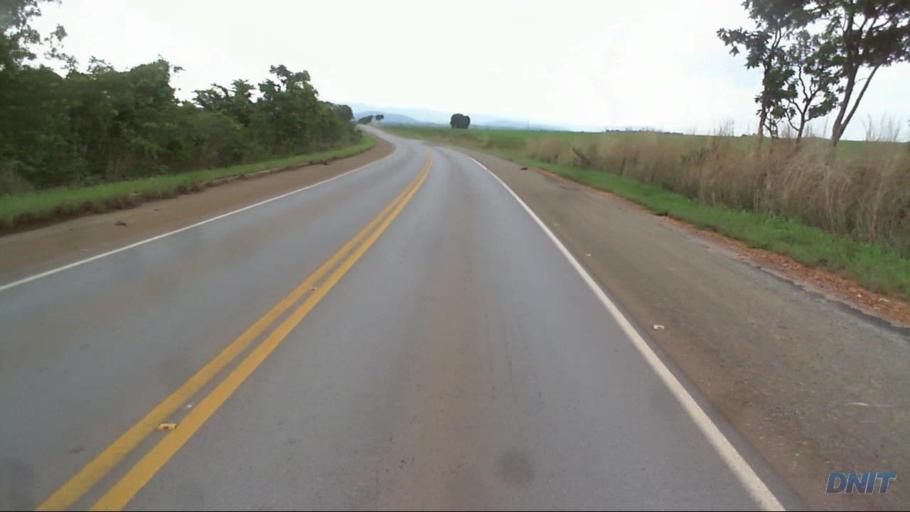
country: BR
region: Goias
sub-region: Barro Alto
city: Barro Alto
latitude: -14.7894
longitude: -49.0537
